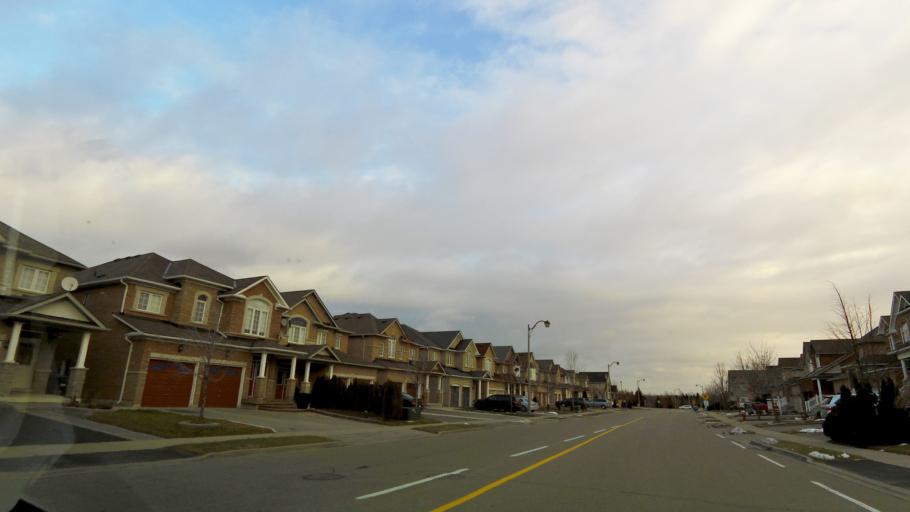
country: CA
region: Ontario
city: Brampton
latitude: 43.7570
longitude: -79.7287
